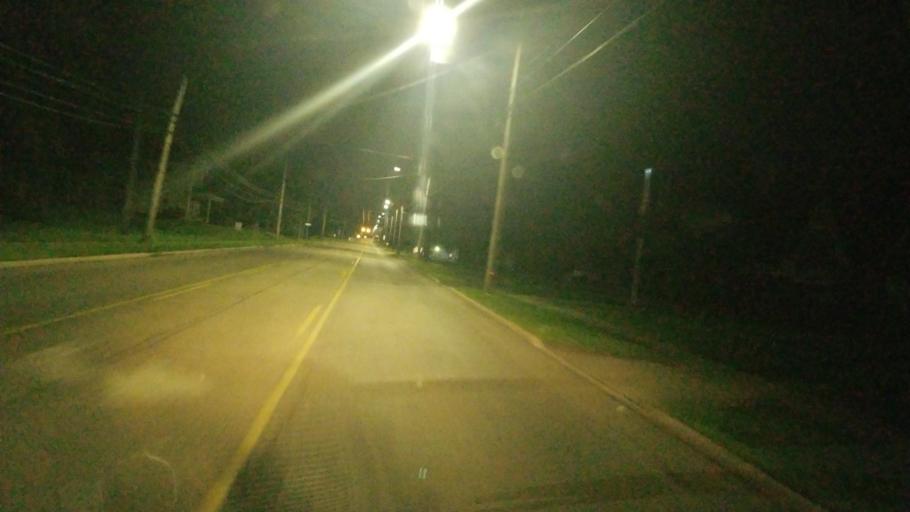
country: US
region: Ohio
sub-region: Trumbull County
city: McKinley Heights
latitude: 41.1823
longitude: -80.7354
